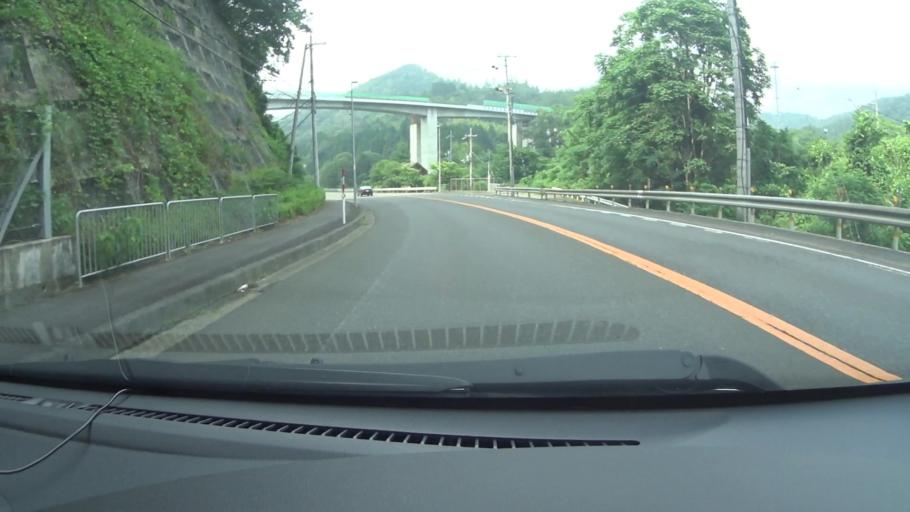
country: JP
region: Kyoto
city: Maizuru
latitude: 35.3703
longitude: 135.3212
